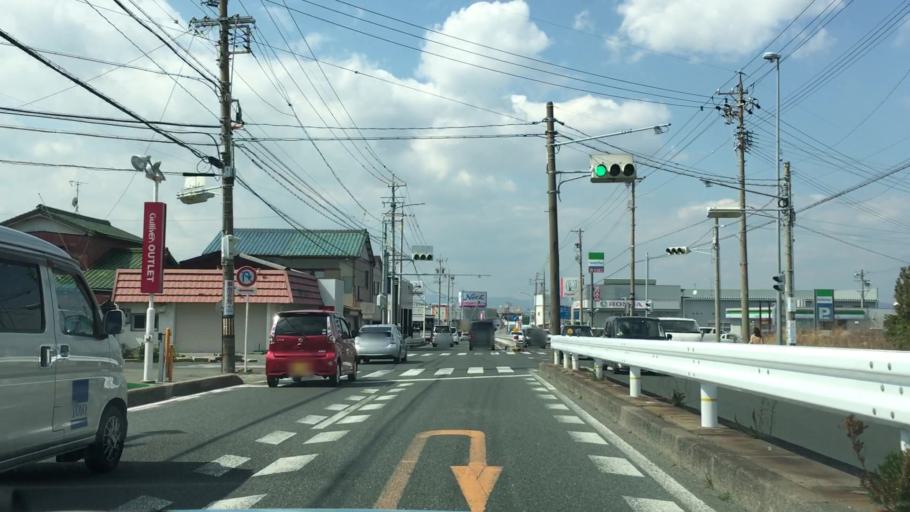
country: JP
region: Aichi
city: Toyohashi
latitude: 34.7424
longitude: 137.4177
